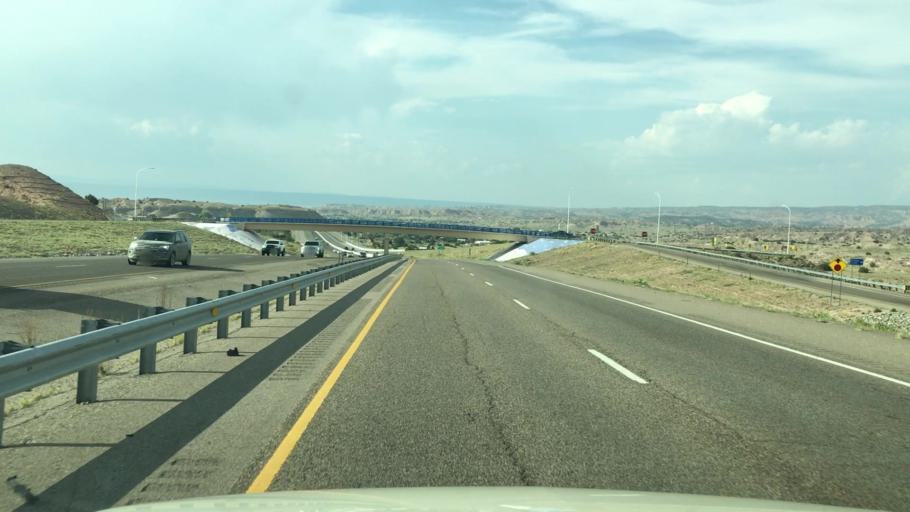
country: US
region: New Mexico
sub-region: Santa Fe County
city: Pojoaque
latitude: 35.9268
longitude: -106.0173
